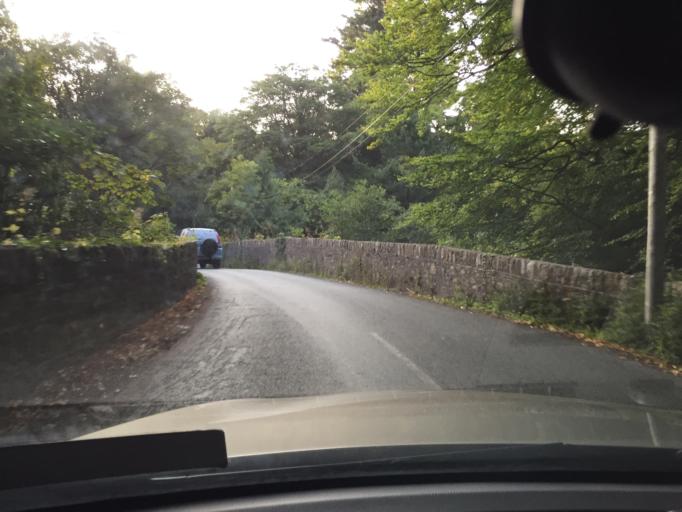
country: IE
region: Leinster
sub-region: Wicklow
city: Enniskerry
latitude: 53.1821
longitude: -6.1735
